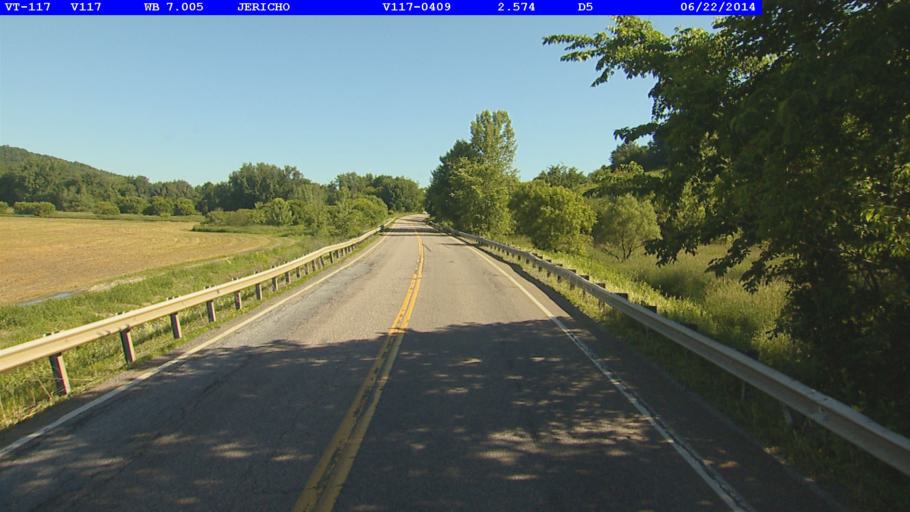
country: US
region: Vermont
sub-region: Chittenden County
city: Williston
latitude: 44.4387
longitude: -73.0198
